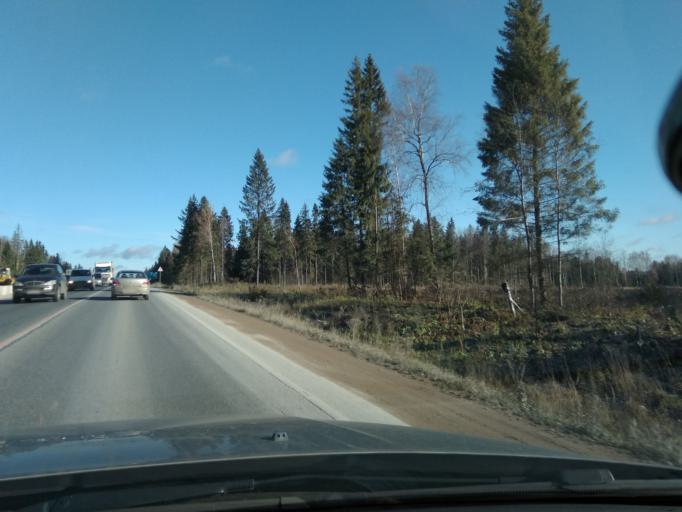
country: RU
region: Moskovskaya
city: Snegiri
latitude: 55.9384
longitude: 36.9607
